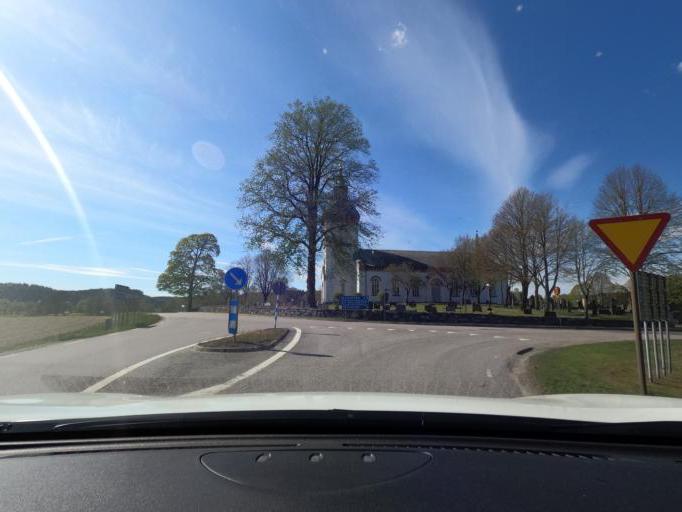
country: SE
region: Vaestra Goetaland
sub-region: Harryda Kommun
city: Ravlanda
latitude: 57.6493
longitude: 12.4900
